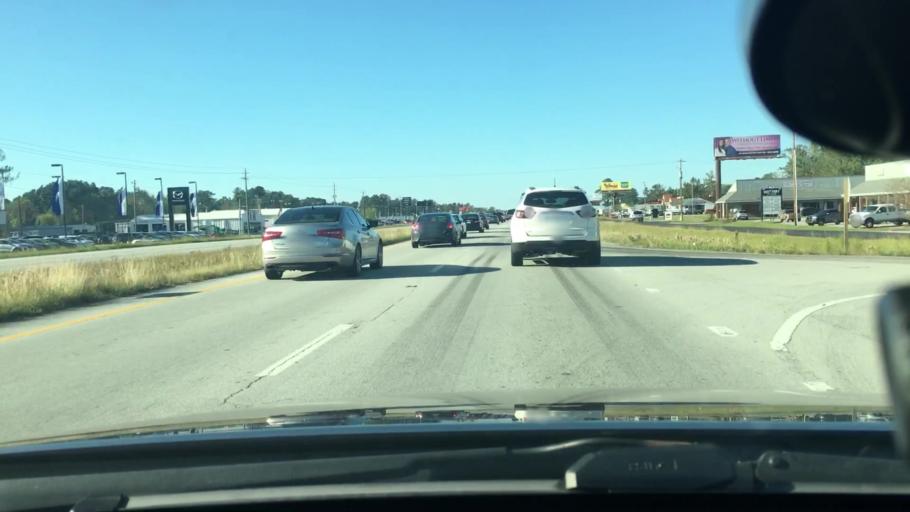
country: US
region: North Carolina
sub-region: Craven County
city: James City
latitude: 35.0681
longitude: -77.0241
